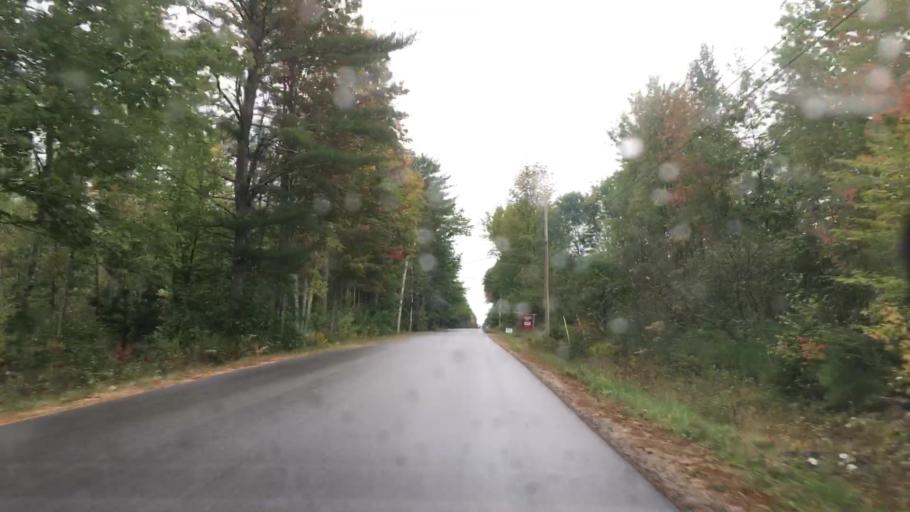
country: US
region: Maine
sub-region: Cumberland County
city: Harrison
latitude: 44.0937
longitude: -70.6566
